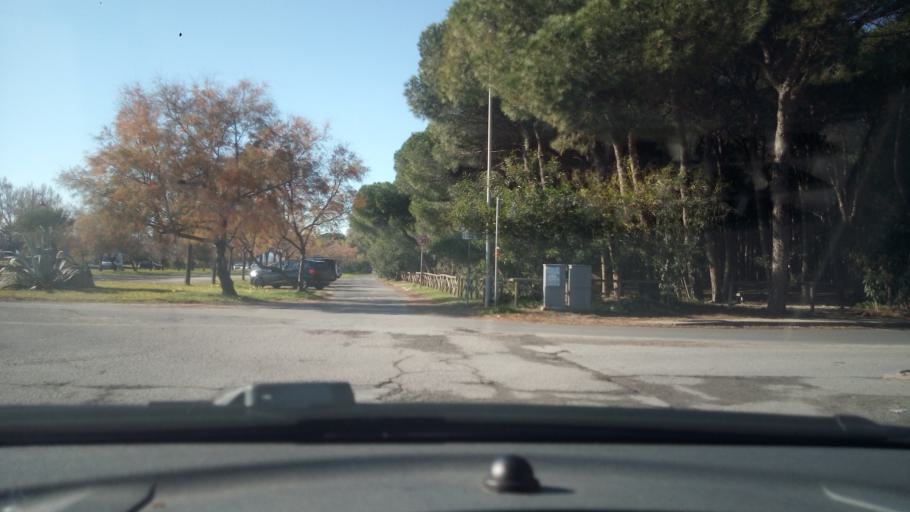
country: IT
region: Calabria
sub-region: Provincia di Catanzaro
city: Barone
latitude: 38.8311
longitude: 16.6433
